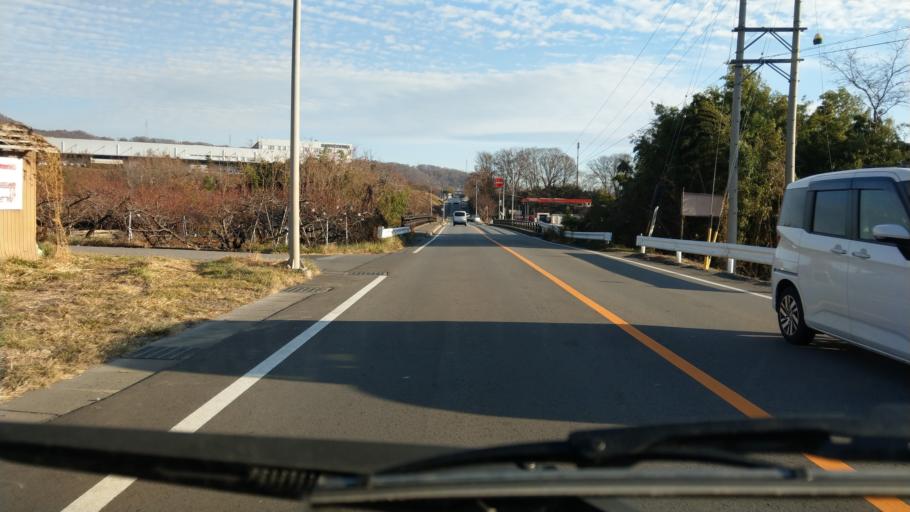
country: JP
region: Nagano
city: Ueda
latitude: 36.3990
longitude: 138.2932
